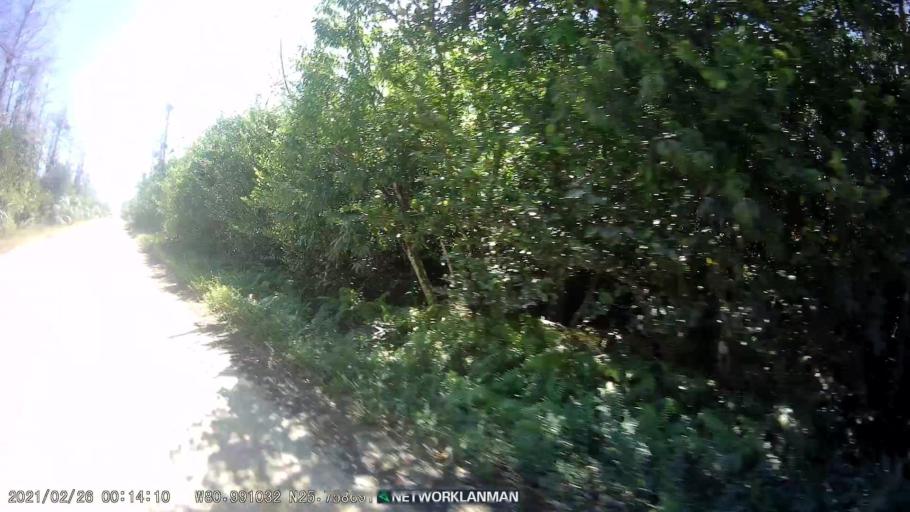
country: US
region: Florida
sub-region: Miami-Dade County
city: The Hammocks
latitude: 25.7584
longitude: -80.9902
